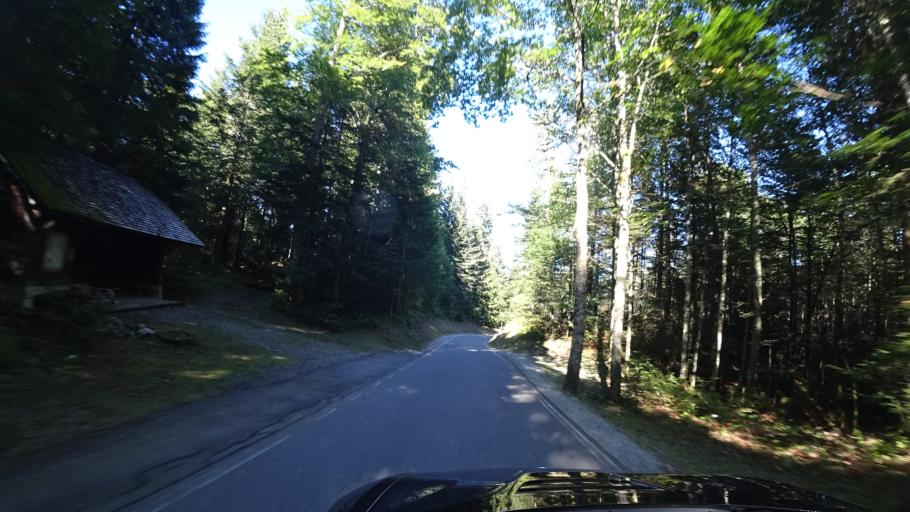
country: CH
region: Obwalden
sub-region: Obwalden
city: Lungern
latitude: 46.8286
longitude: 8.1175
